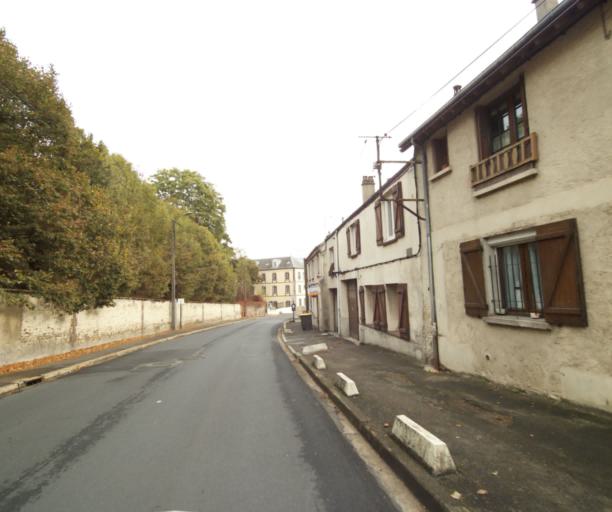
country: FR
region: Centre
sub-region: Departement d'Eure-et-Loir
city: Dreux
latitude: 48.7398
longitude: 1.3580
